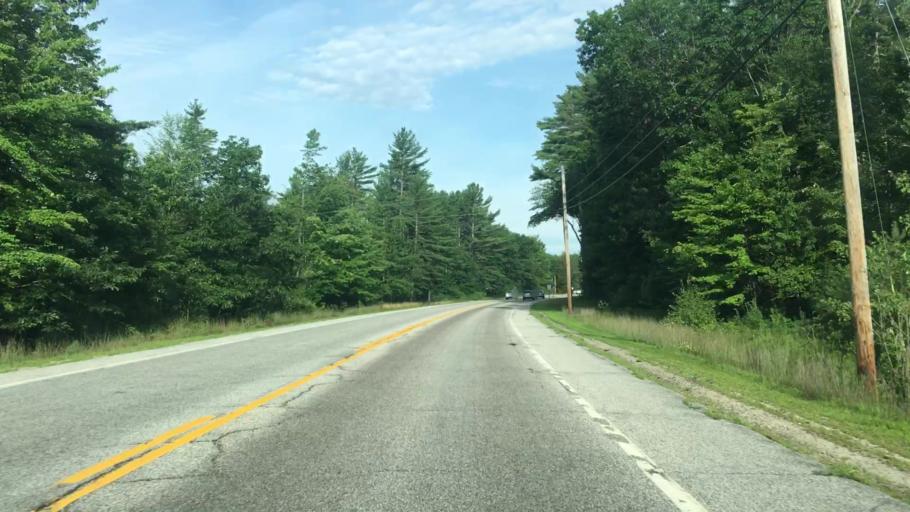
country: US
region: Maine
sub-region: Cumberland County
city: Steep Falls
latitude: 43.7328
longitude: -70.6134
